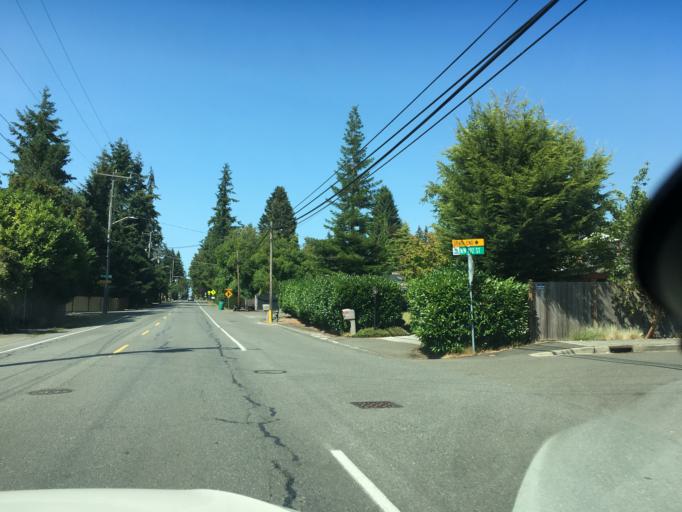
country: US
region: Washington
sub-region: Snohomish County
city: Esperance
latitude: 47.7686
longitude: -122.3666
